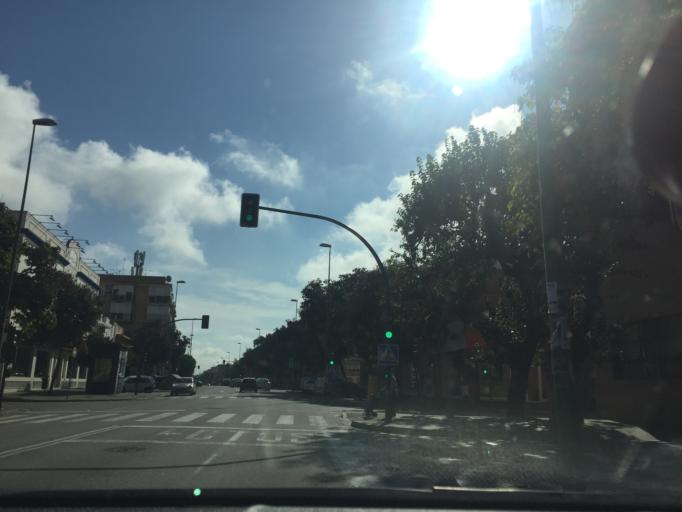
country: ES
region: Andalusia
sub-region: Provincia de Sevilla
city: Sevilla
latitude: 37.3694
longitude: -5.9583
